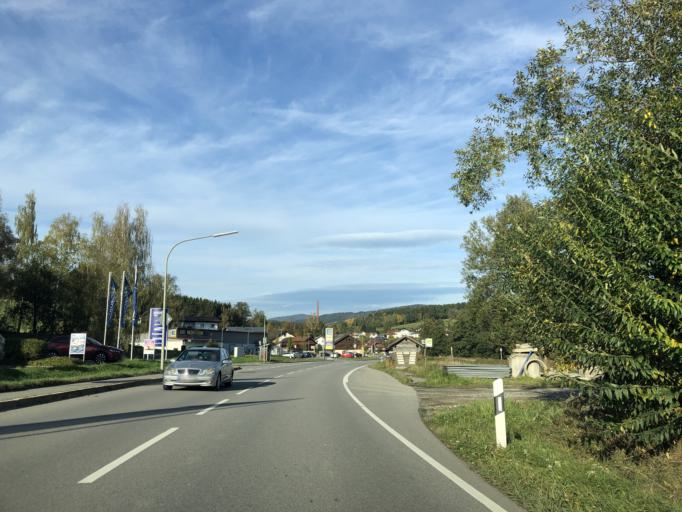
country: DE
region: Bavaria
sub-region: Lower Bavaria
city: Teisnach
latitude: 49.0318
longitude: 12.9913
